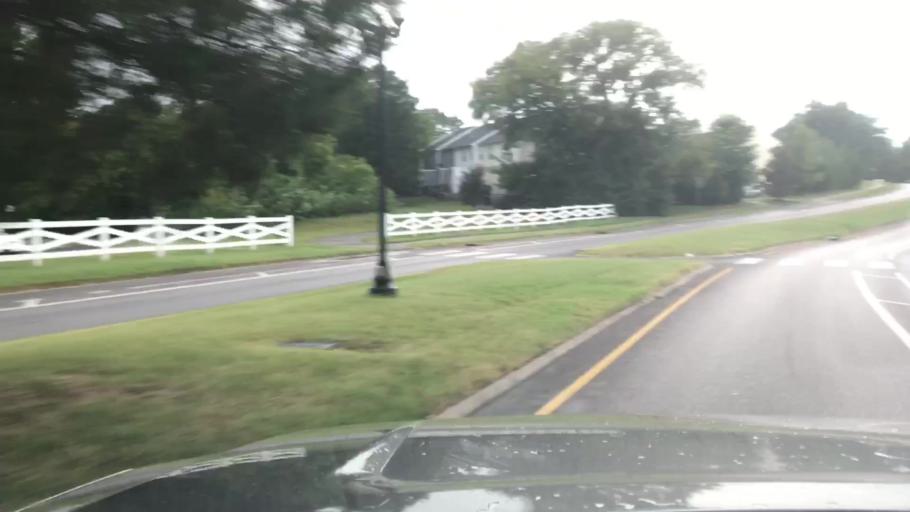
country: US
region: Tennessee
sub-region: Rutherford County
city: La Vergne
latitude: 36.0899
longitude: -86.6314
